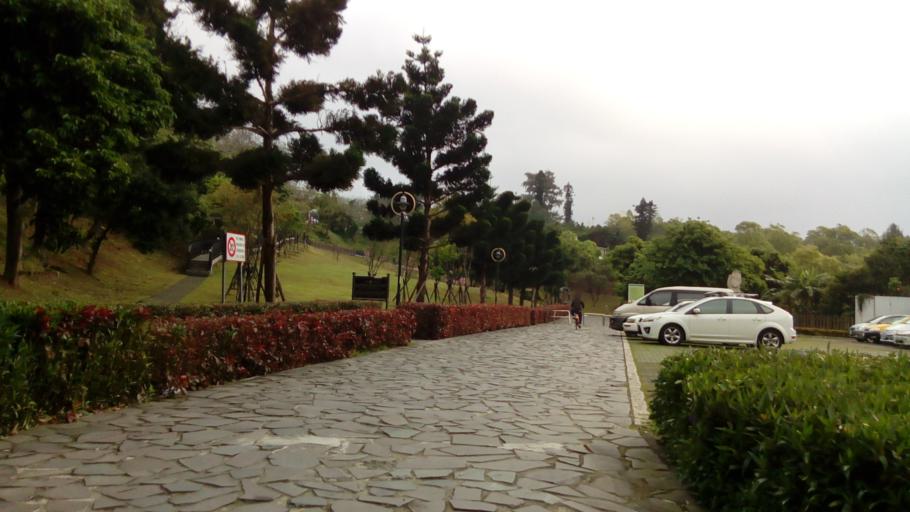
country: TW
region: Taipei
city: Taipei
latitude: 25.1774
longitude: 121.4289
